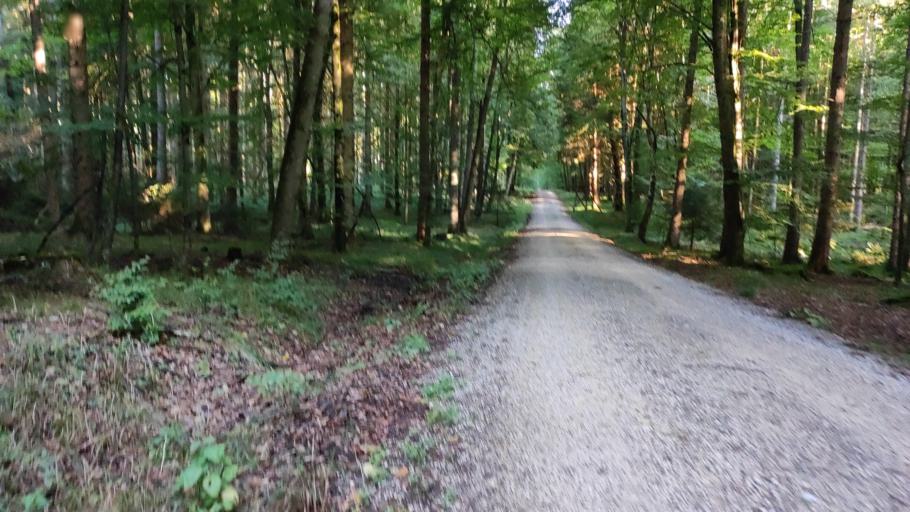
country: DE
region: Bavaria
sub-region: Swabia
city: Welden
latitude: 48.4246
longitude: 10.6414
